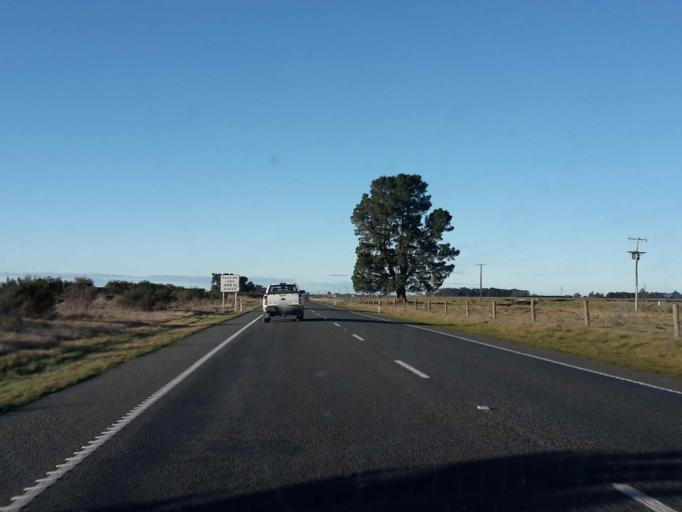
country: NZ
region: Canterbury
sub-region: Ashburton District
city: Tinwald
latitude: -44.0241
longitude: 171.5012
